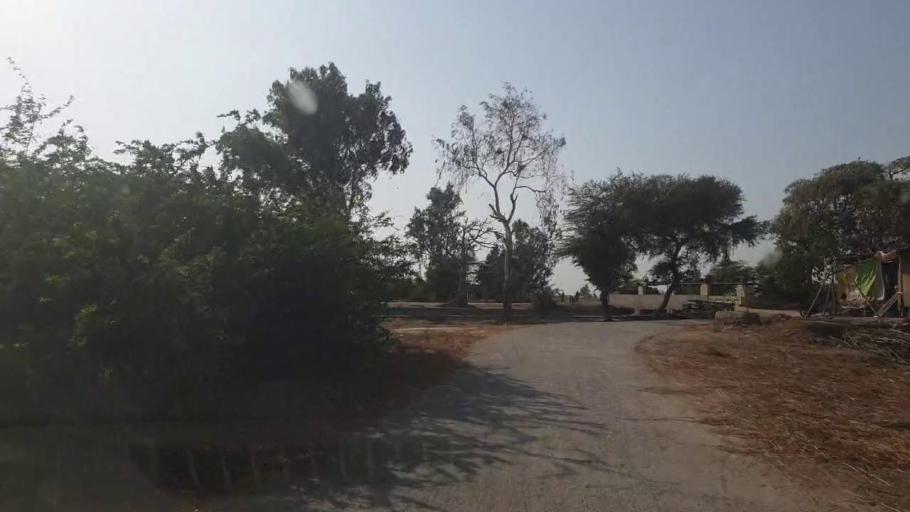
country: PK
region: Sindh
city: Kario
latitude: 24.5764
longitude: 68.4967
